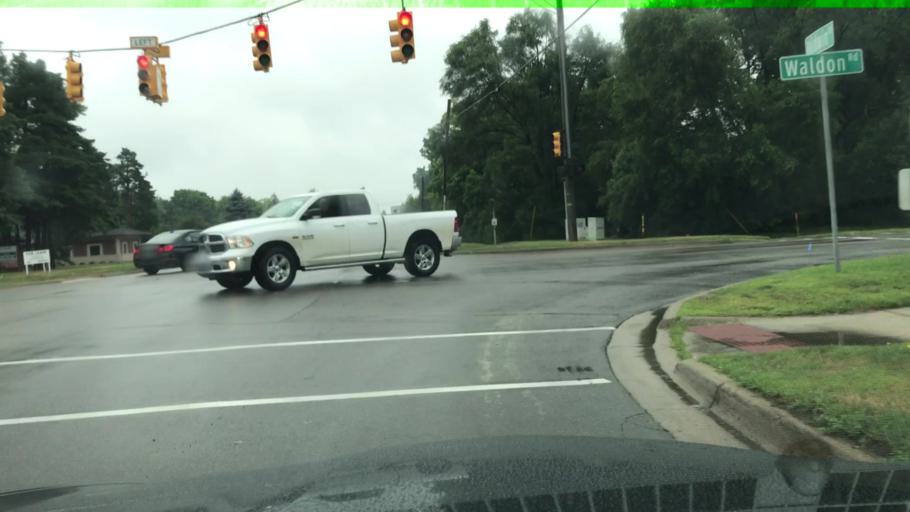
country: US
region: Michigan
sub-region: Oakland County
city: Lake Orion
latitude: 42.7360
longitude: -83.3080
